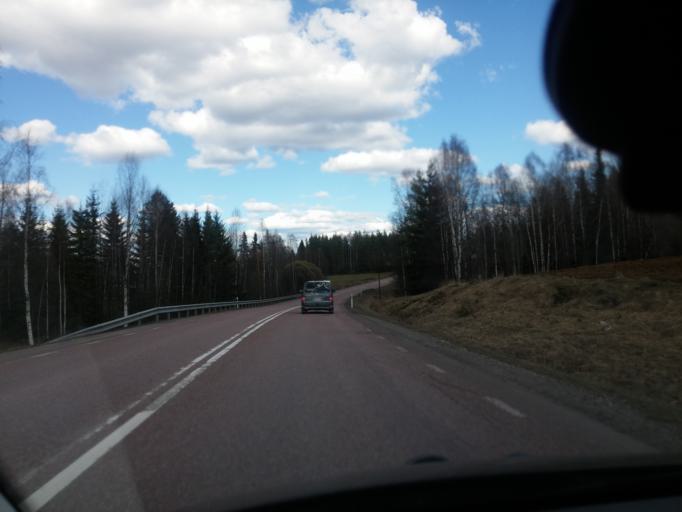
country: SE
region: Gaevleborg
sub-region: Ljusdals Kommun
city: Farila
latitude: 61.8120
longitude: 15.9577
